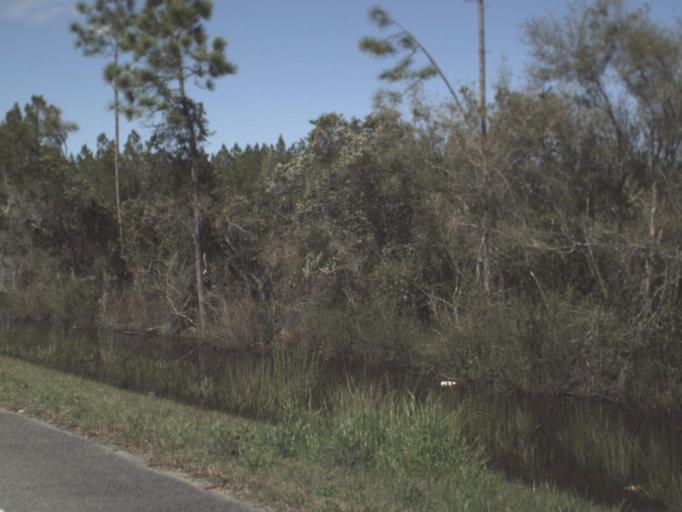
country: US
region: Florida
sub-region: Gulf County
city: Wewahitchka
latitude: 29.9867
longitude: -85.1684
